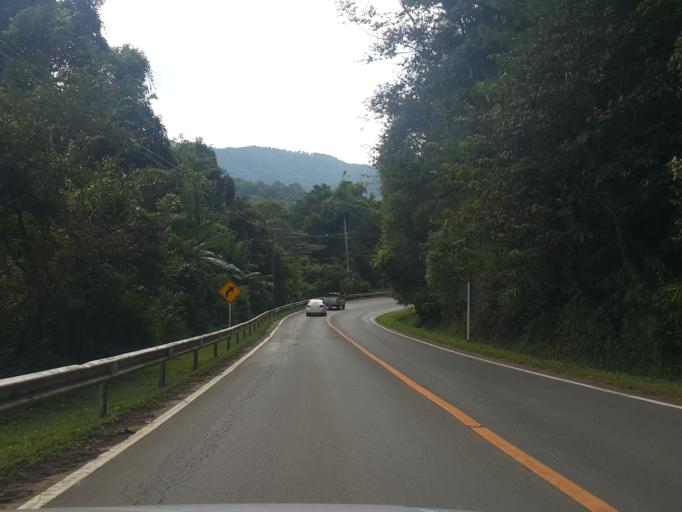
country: TH
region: Chiang Mai
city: Chom Thong
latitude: 18.5423
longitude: 98.5489
